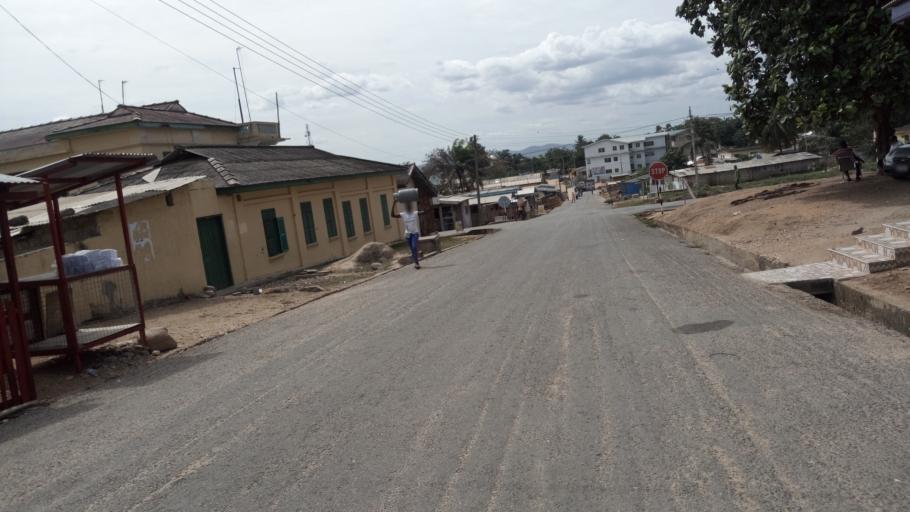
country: GH
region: Central
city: Winneba
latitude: 5.3481
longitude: -0.6238
